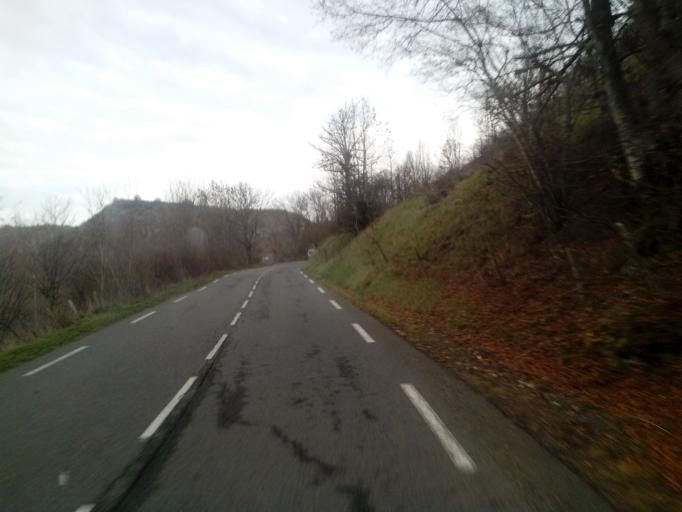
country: FR
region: Languedoc-Roussillon
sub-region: Departement de la Lozere
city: Florac
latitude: 44.2729
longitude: 3.6006
